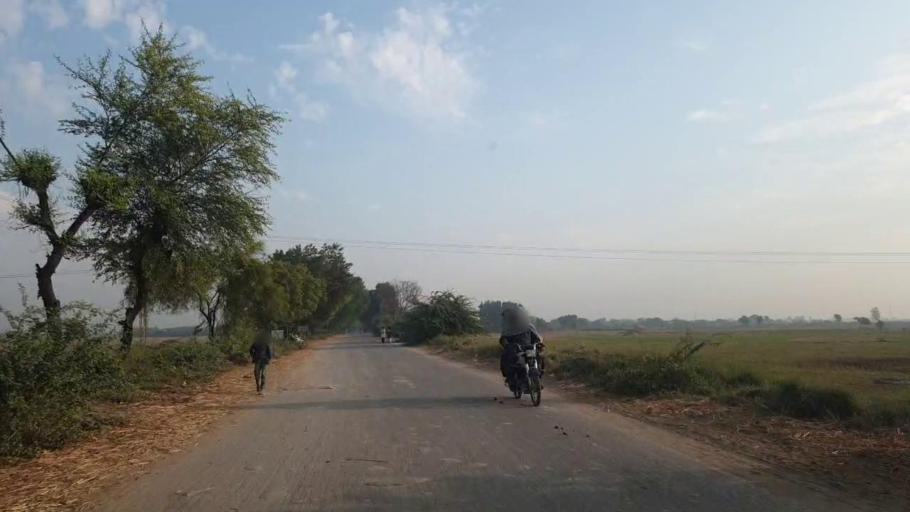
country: PK
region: Sindh
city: Tando Bago
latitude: 24.7580
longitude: 68.9533
